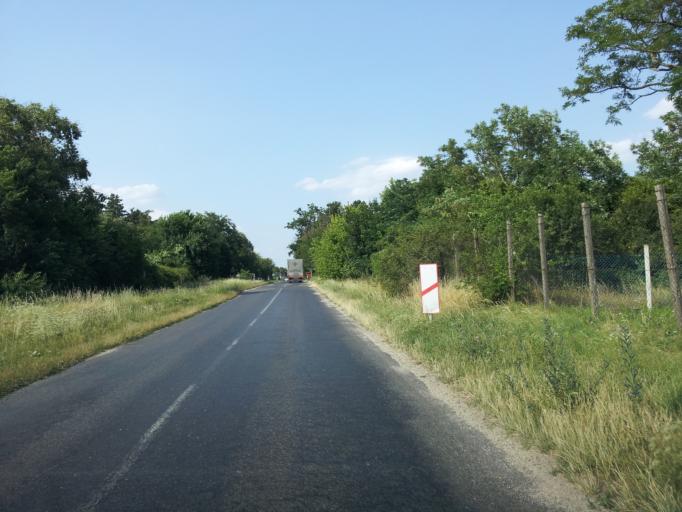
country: HU
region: Veszprem
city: Berhida
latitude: 47.1027
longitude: 18.0963
